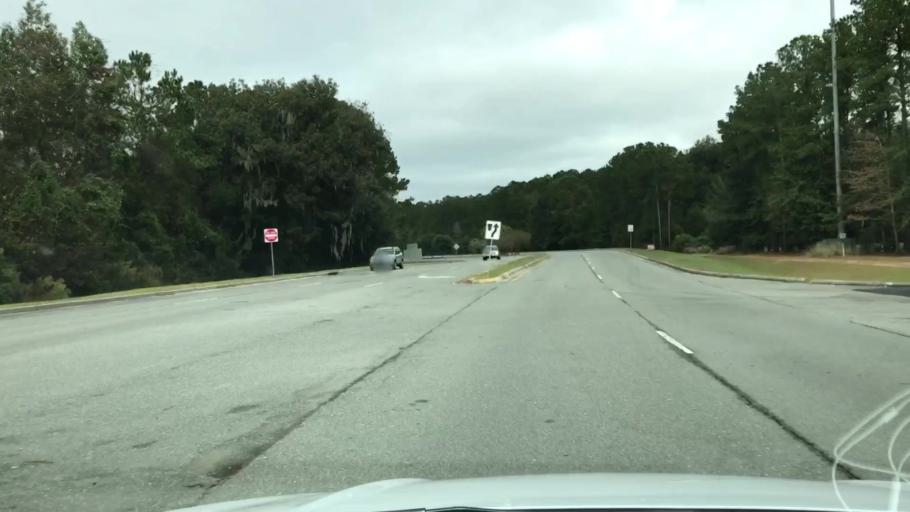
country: US
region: South Carolina
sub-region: Beaufort County
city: Bluffton
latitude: 32.2529
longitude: -80.9016
